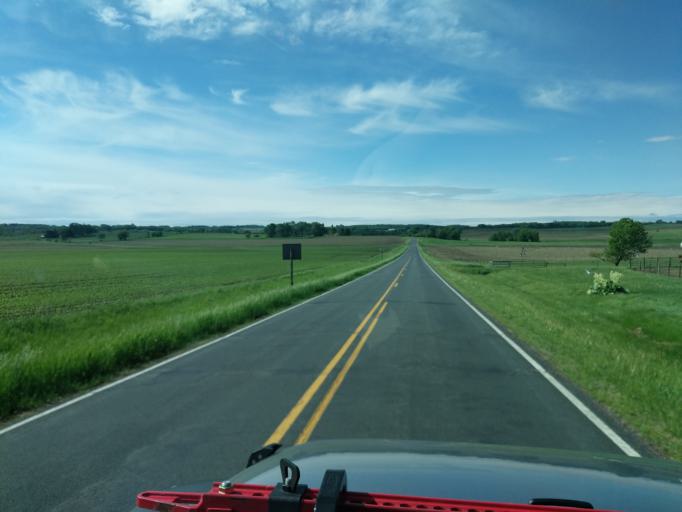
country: US
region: Wisconsin
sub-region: Saint Croix County
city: Hammond
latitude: 44.9125
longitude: -92.4864
